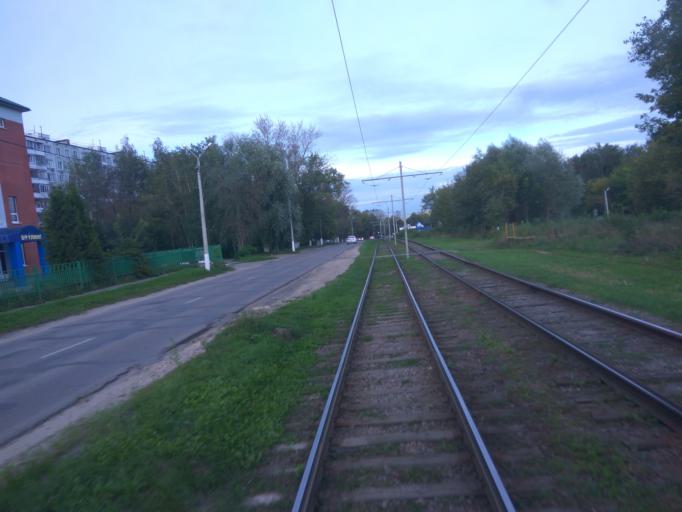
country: RU
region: Moskovskaya
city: Kolomna
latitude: 55.0743
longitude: 38.7973
